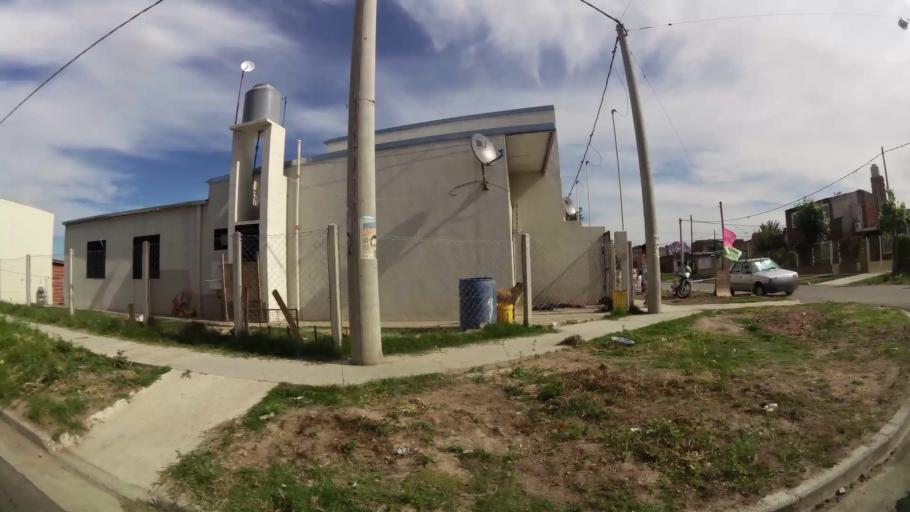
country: AR
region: Santa Fe
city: Granadero Baigorria
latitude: -32.9127
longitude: -60.7176
